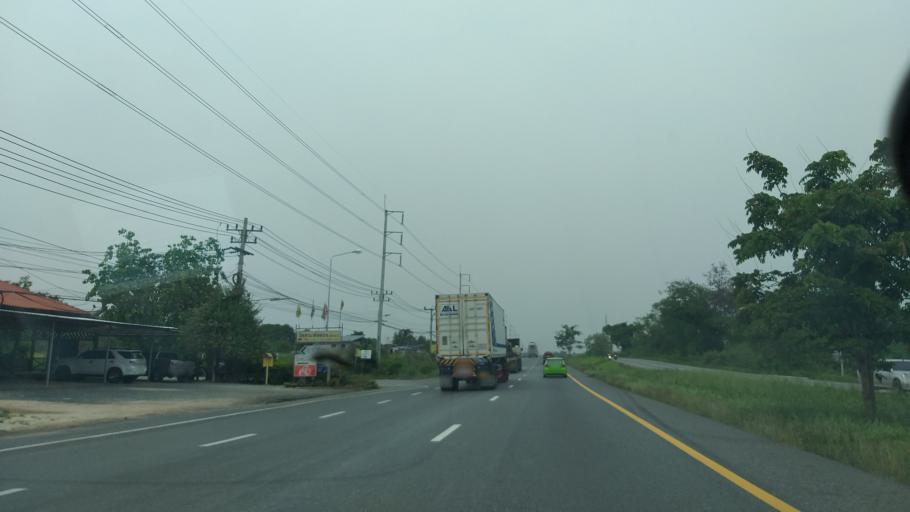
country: TH
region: Chon Buri
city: Ko Chan
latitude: 13.4332
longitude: 101.2829
